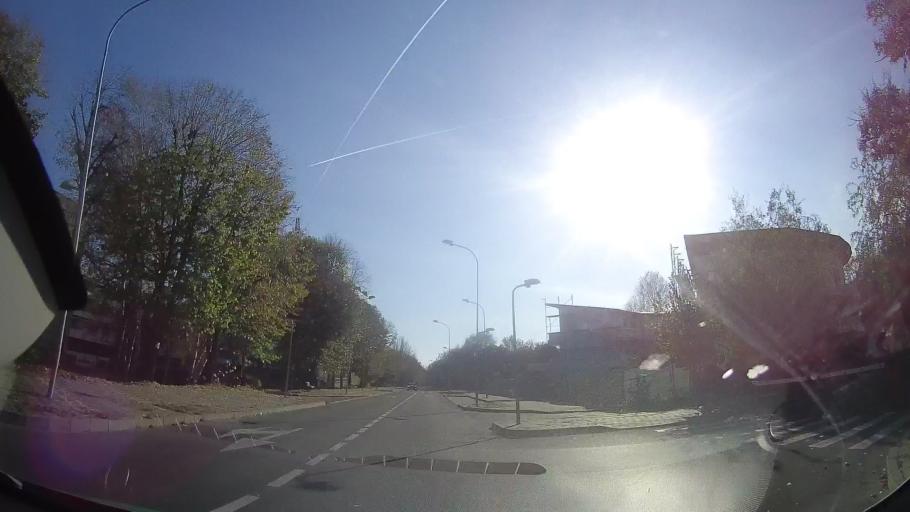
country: RO
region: Constanta
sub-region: Comuna Douazeci si Trei August
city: Douazeci si Trei August
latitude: 43.8795
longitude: 28.6031
